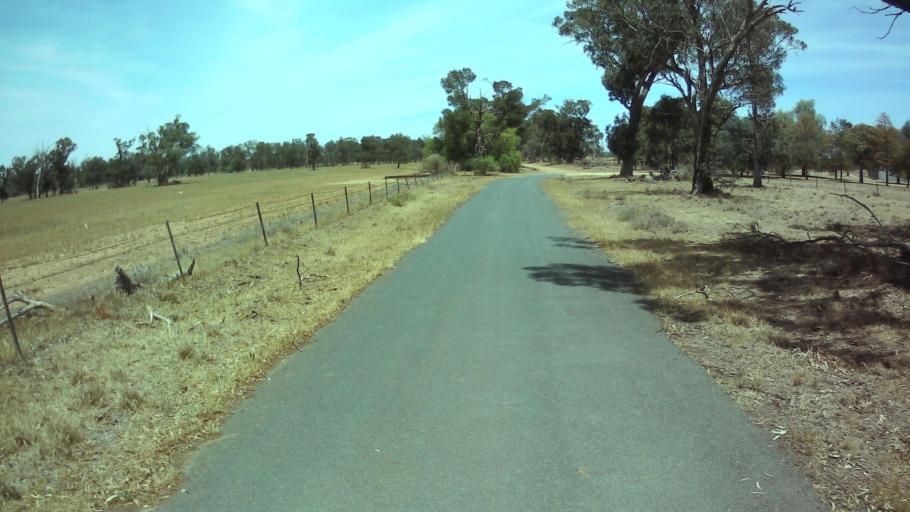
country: AU
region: New South Wales
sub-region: Weddin
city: Grenfell
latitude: -34.0287
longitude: 147.9402
